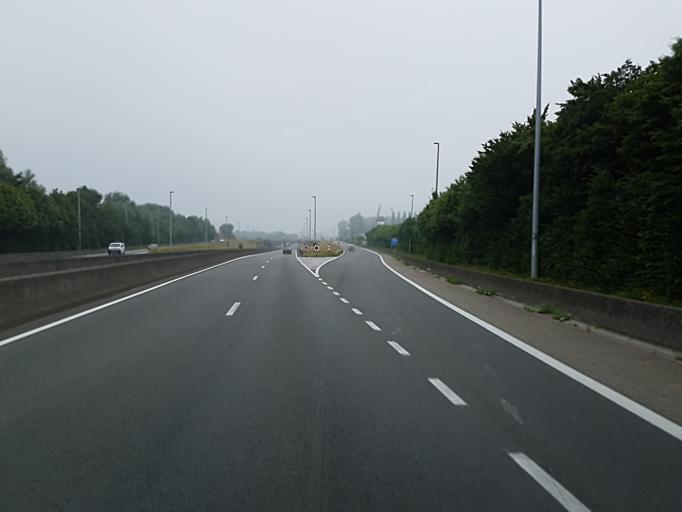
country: FR
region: Nord-Pas-de-Calais
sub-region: Departement du Nord
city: Halluin
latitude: 50.7953
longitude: 3.1372
